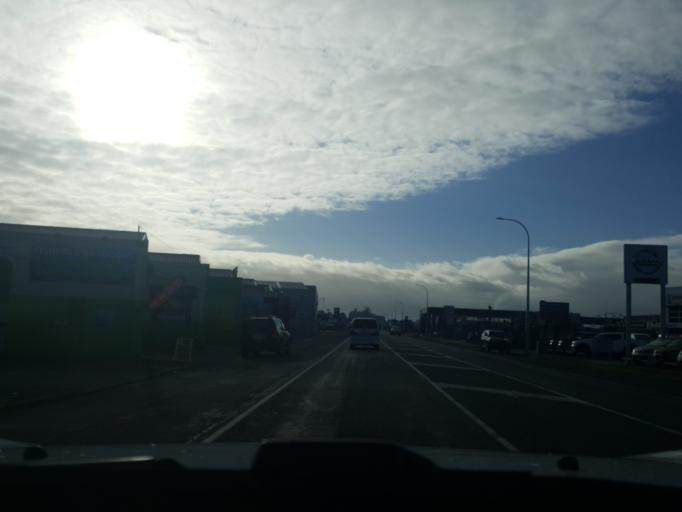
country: NZ
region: Waikato
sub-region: Waipa District
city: Cambridge
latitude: -37.6616
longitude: 175.5179
